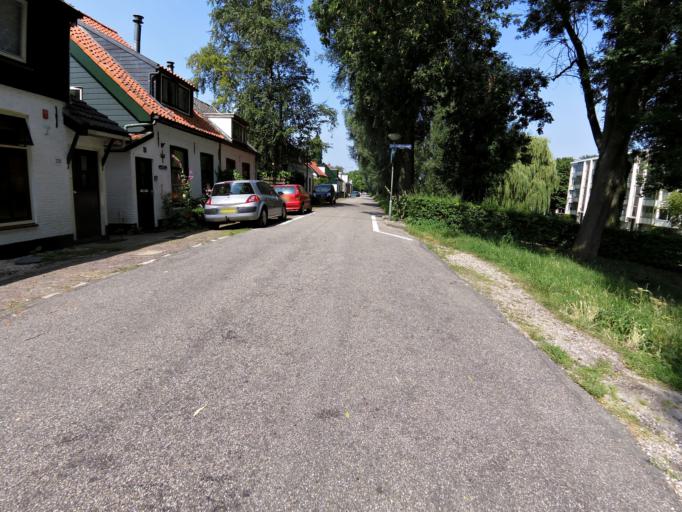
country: NL
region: South Holland
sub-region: Gemeente Dordrecht
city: Dordrecht
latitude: 51.7927
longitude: 4.6589
